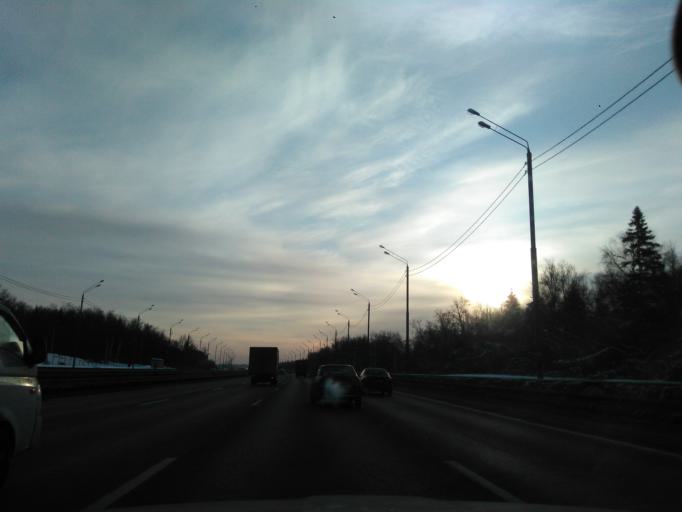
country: RU
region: Moskovskaya
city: Yershovo
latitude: 55.8189
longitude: 36.9482
